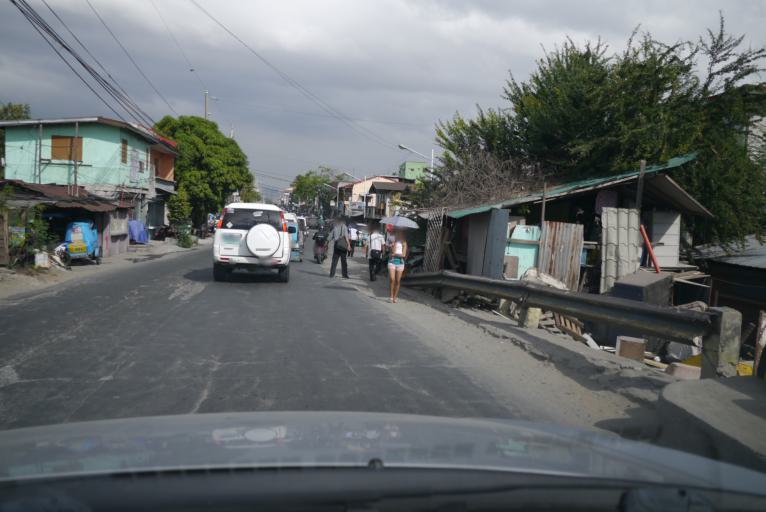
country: PH
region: Calabarzon
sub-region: Province of Rizal
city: Cainta
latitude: 14.5643
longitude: 121.1101
